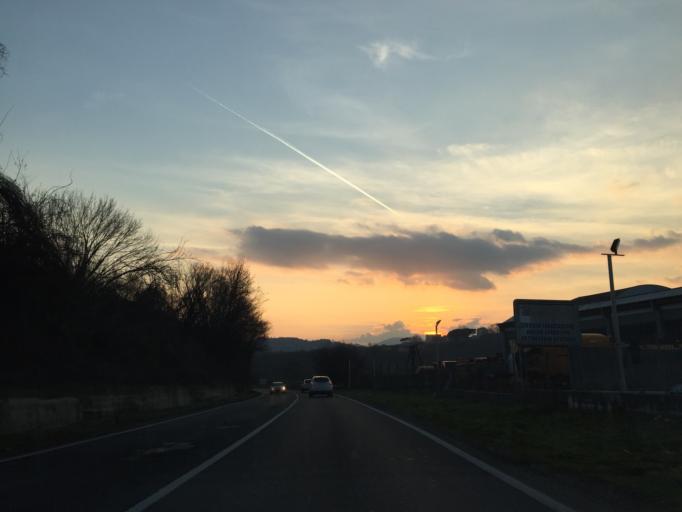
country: IT
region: Campania
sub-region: Provincia di Avellino
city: Atripalda
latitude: 40.9116
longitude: 14.8149
